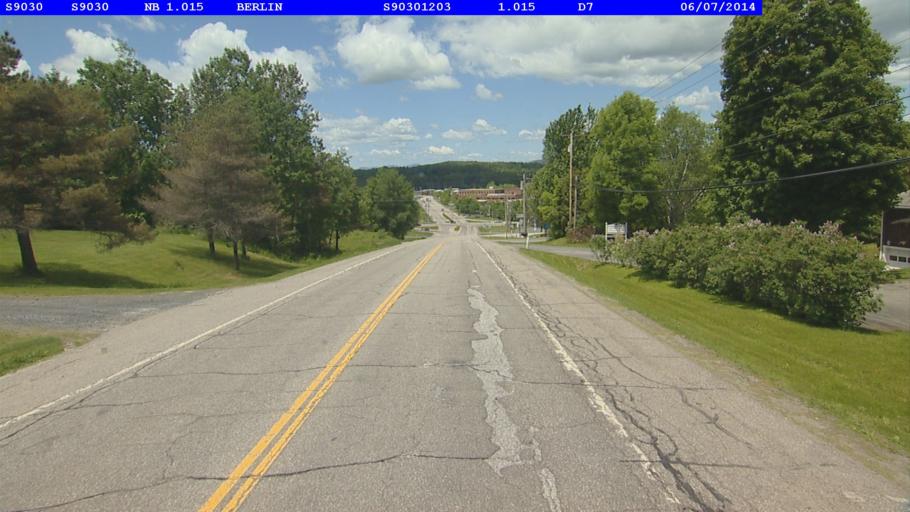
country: US
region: Vermont
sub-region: Washington County
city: Montpelier
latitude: 44.2161
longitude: -72.5574
